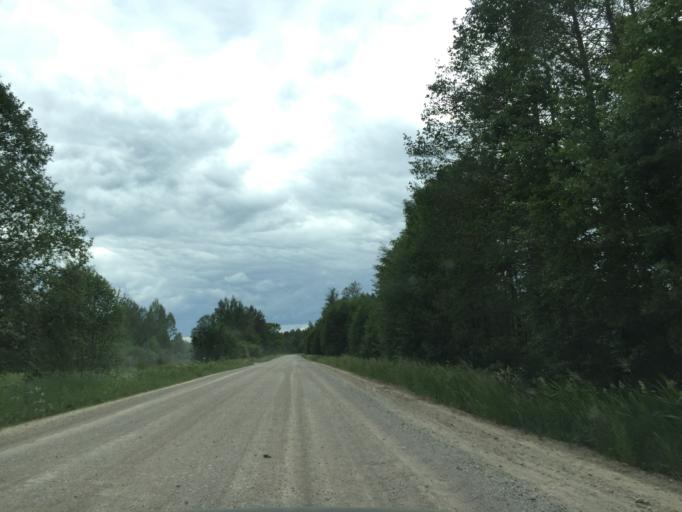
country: LV
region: Vilanu
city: Vilani
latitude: 56.4425
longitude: 27.0734
